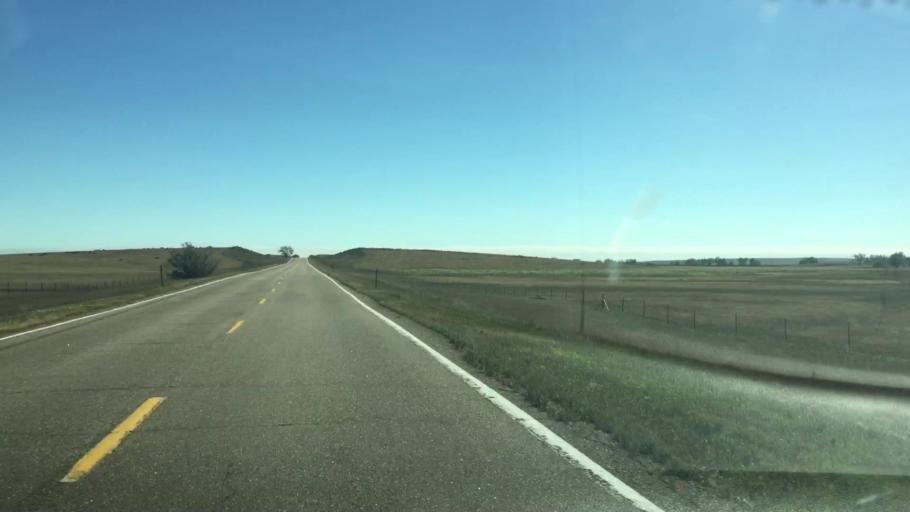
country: US
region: Colorado
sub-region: Lincoln County
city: Limon
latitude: 39.2944
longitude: -103.9036
